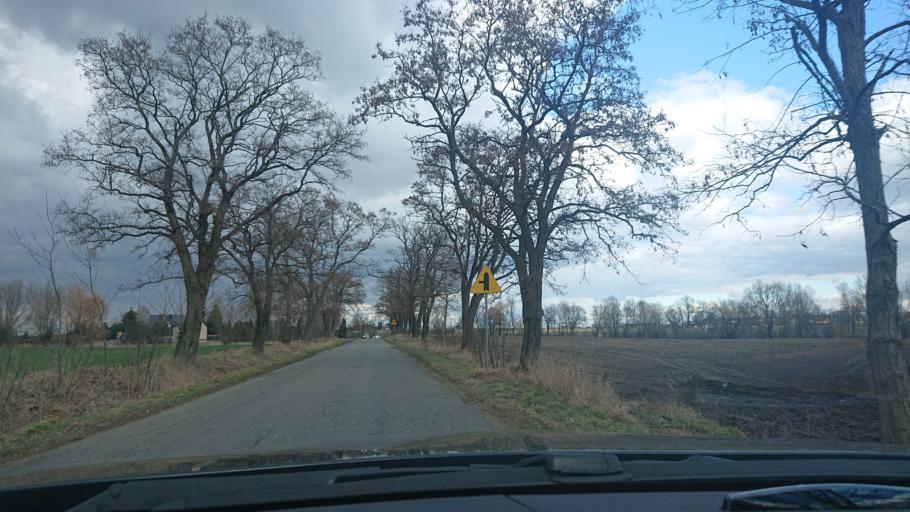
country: PL
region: Greater Poland Voivodeship
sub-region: Powiat gnieznienski
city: Trzemeszno
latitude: 52.5802
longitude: 17.7120
